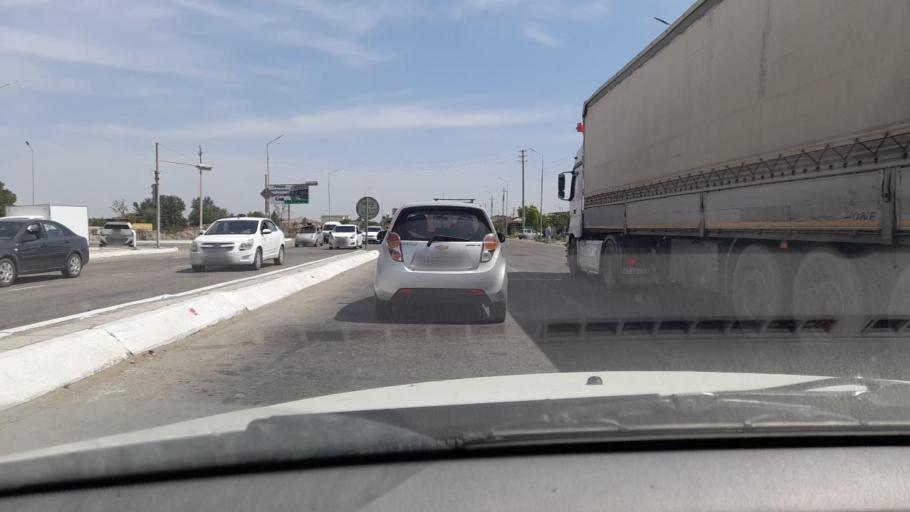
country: UZ
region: Bukhara
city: Galaosiyo
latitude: 39.8633
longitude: 64.4457
